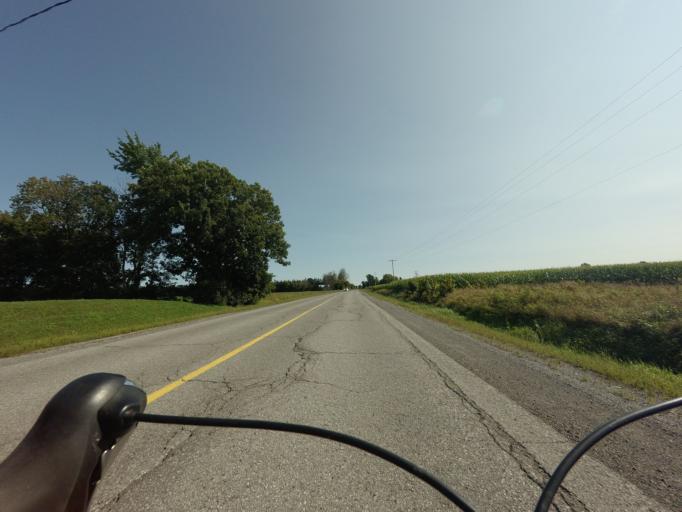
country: CA
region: Ontario
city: Carleton Place
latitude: 45.3532
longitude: -76.1160
